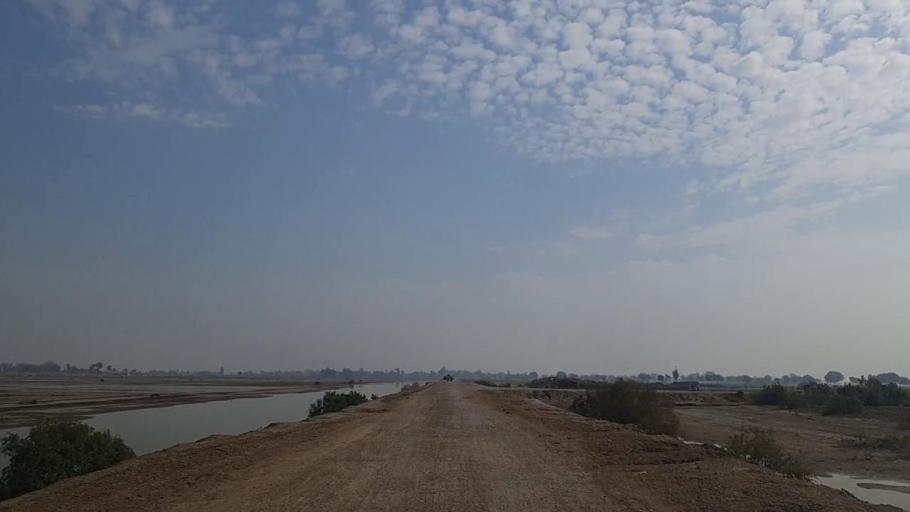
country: PK
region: Sindh
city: Daur
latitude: 26.3840
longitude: 68.3815
